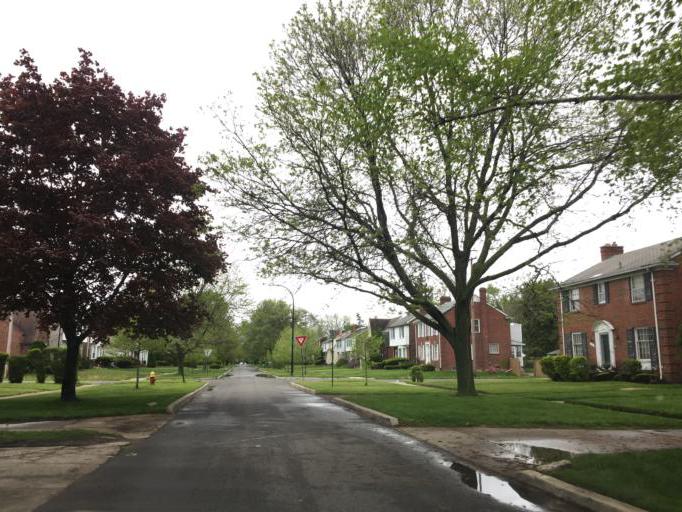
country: US
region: Michigan
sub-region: Oakland County
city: Oak Park
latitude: 42.4142
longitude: -83.2200
